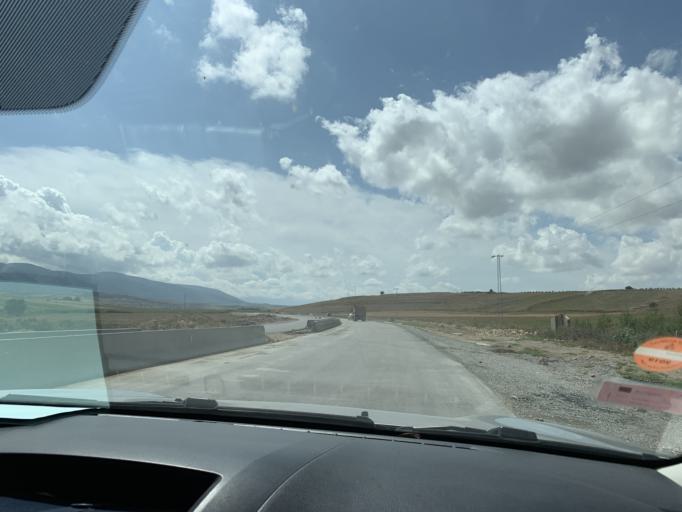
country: TN
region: Silyanah
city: Bu `Aradah
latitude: 36.1587
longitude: 9.6402
